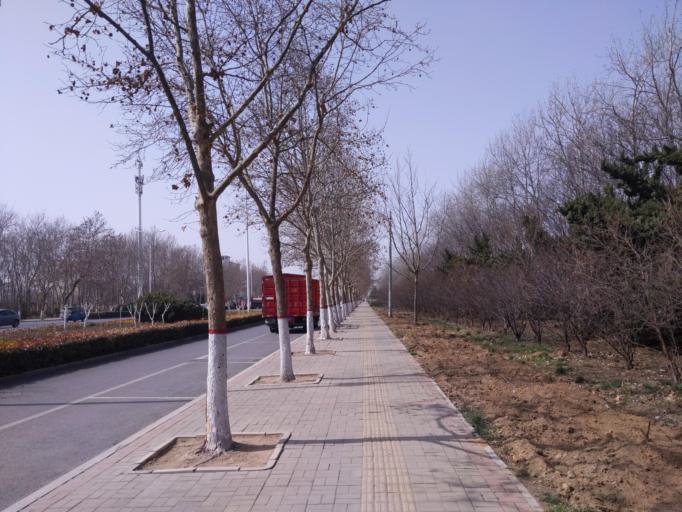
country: CN
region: Henan Sheng
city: Puyang
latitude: 35.7746
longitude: 114.9534
